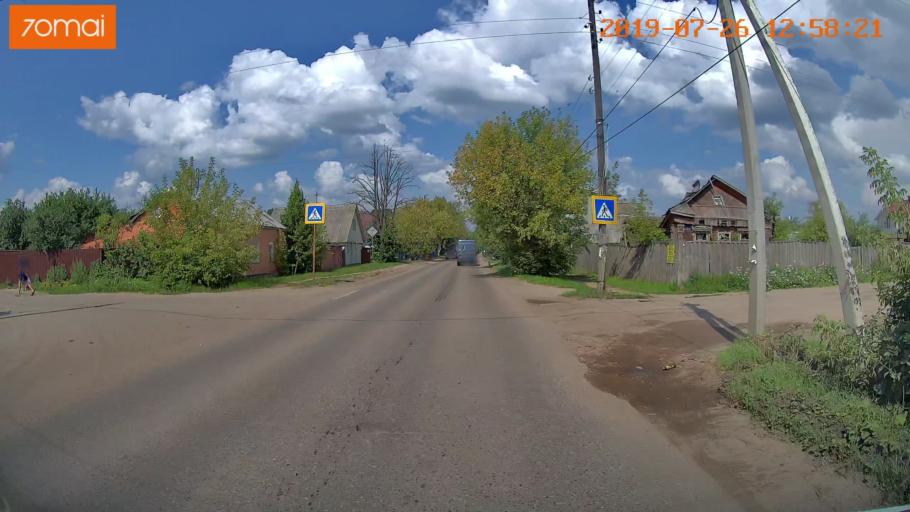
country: RU
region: Ivanovo
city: Bogorodskoye
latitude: 57.0236
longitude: 41.0208
